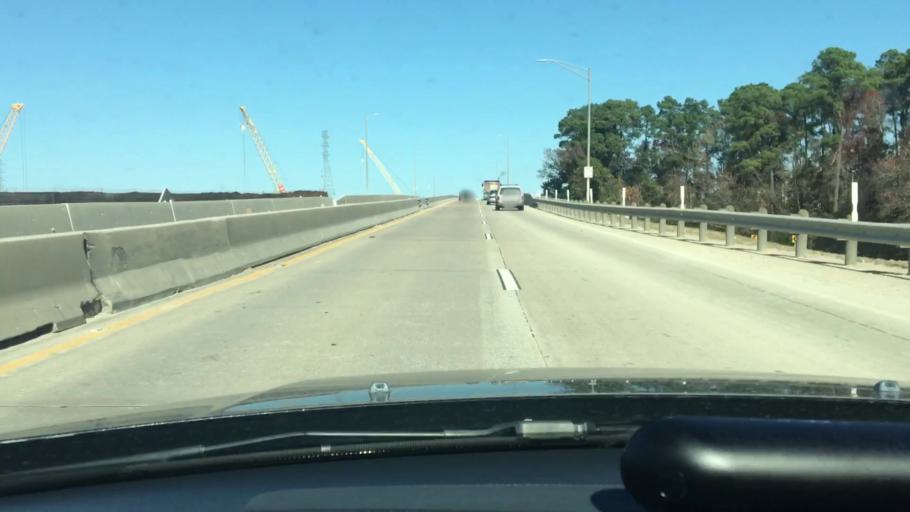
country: US
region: Texas
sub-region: Harris County
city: Cloverleaf
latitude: 29.7525
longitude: -95.1459
